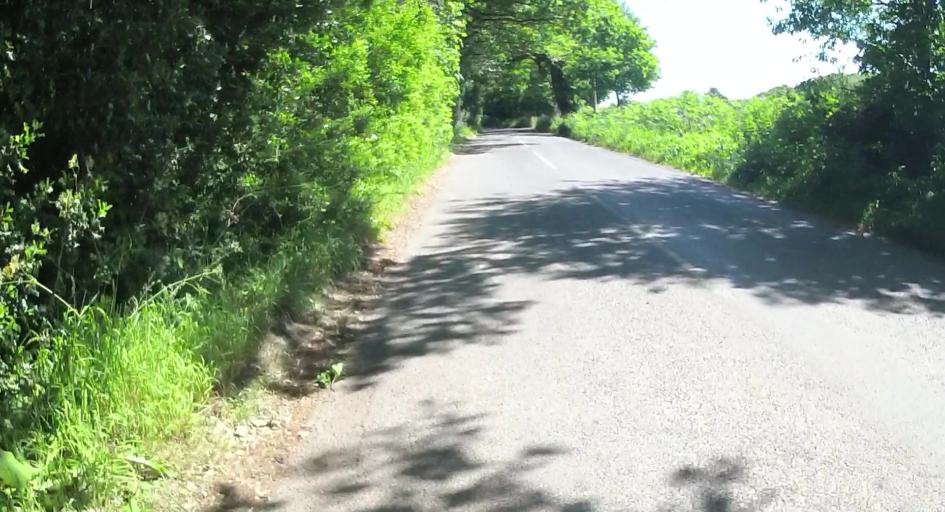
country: GB
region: England
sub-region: Hampshire
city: Hook
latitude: 51.3108
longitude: -0.9843
